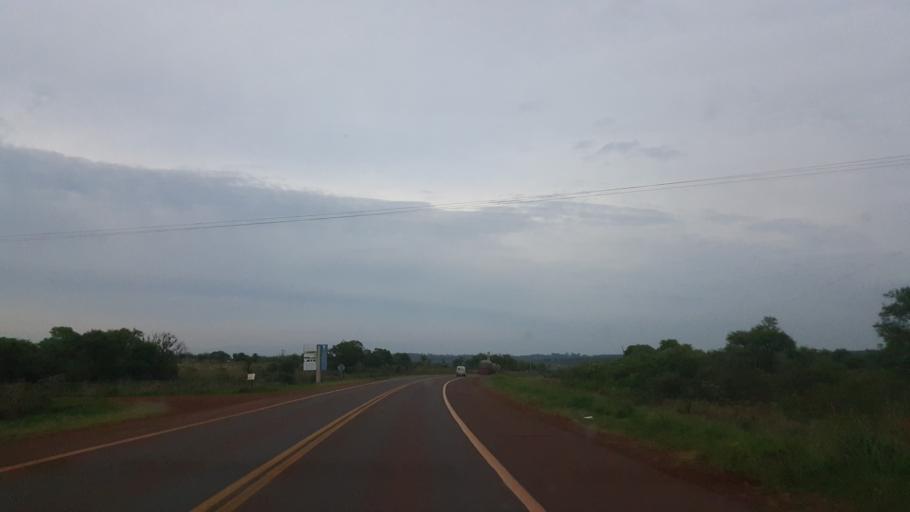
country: AR
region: Misiones
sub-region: Departamento de Apostoles
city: San Jose
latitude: -27.7592
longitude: -55.7890
